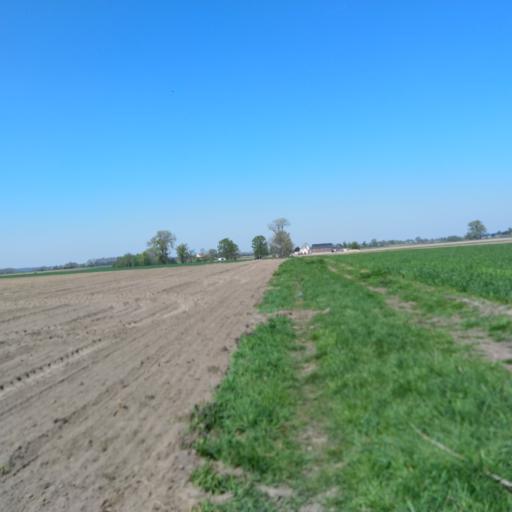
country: BE
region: Wallonia
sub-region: Province du Hainaut
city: Jurbise
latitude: 50.5122
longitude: 3.9159
